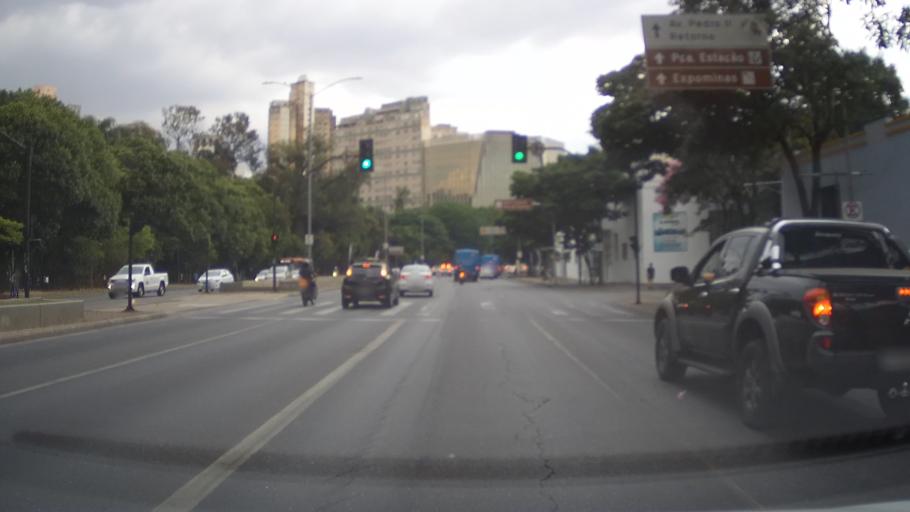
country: BR
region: Minas Gerais
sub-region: Belo Horizonte
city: Belo Horizonte
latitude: -19.9216
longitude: -43.9329
